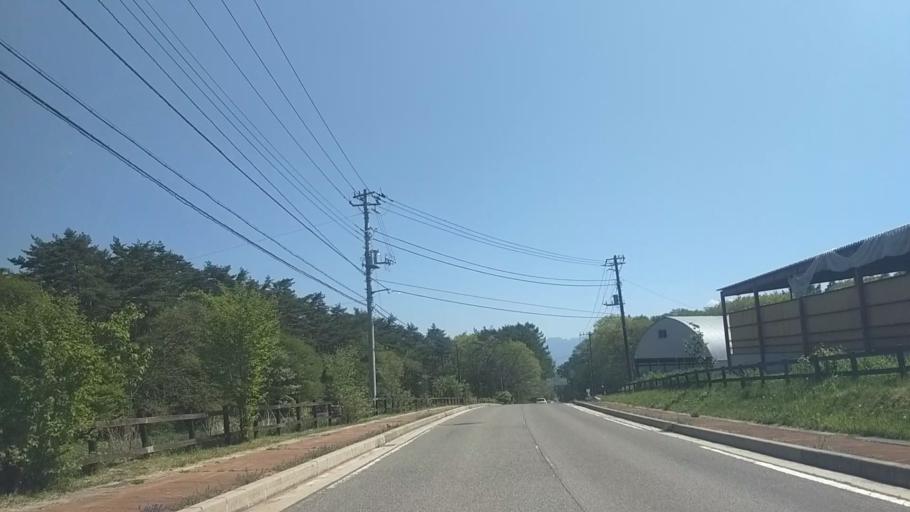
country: JP
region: Yamanashi
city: Nirasaki
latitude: 35.9157
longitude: 138.4340
